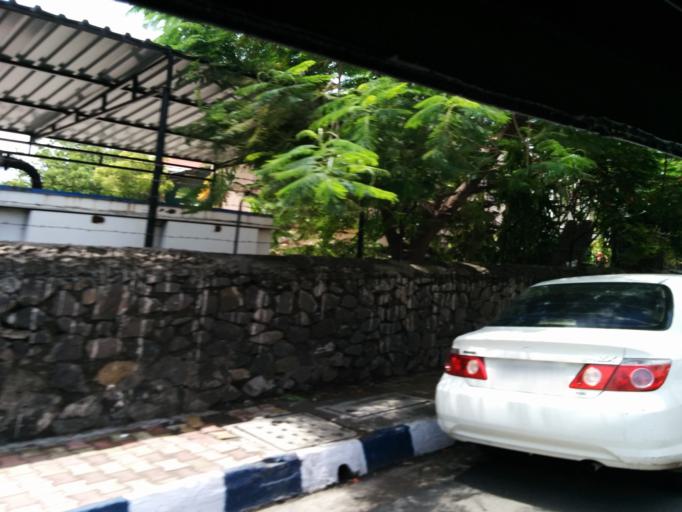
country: IN
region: Maharashtra
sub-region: Pune Division
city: Lohogaon
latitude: 18.5711
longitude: 73.9072
